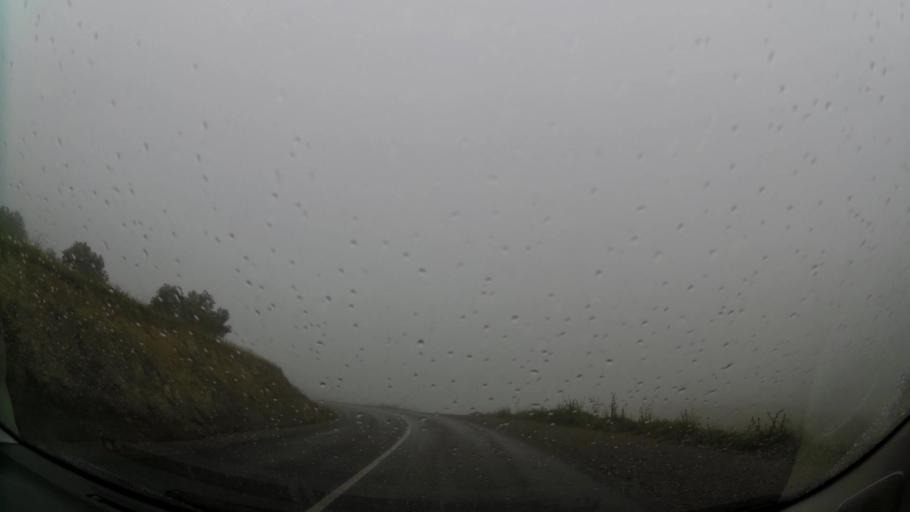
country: MA
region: Oriental
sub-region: Nador
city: Boudinar
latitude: 35.0962
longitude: -3.5326
